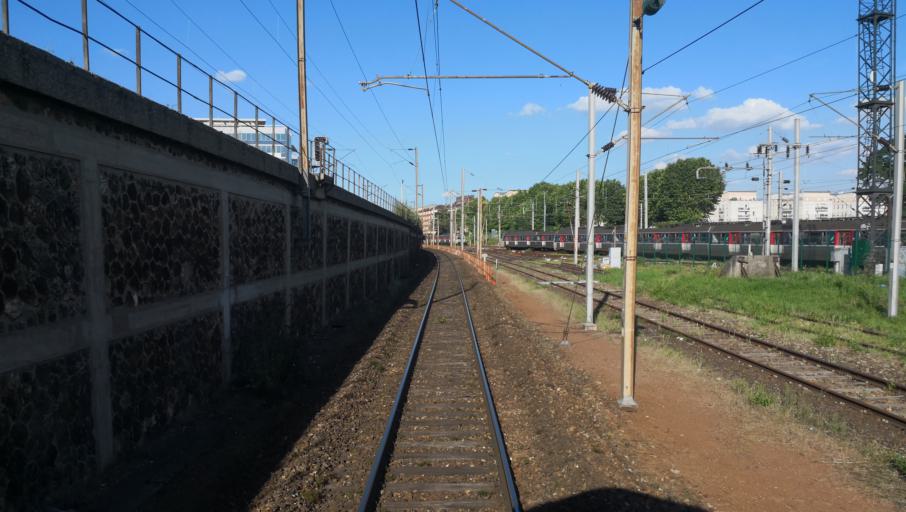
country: FR
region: Ile-de-France
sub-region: Departement des Hauts-de-Seine
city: La Defense
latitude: 48.9067
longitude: 2.2287
